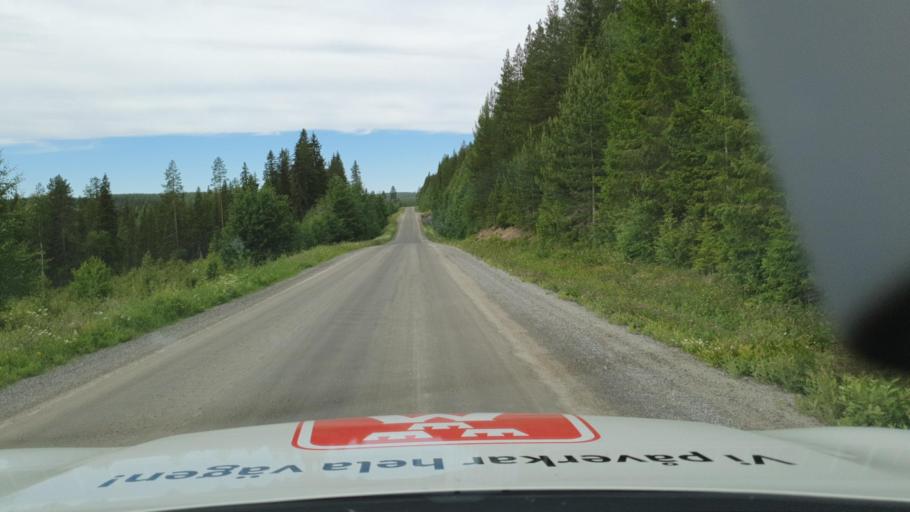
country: SE
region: Vaesterbotten
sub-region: Skelleftea Kommun
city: Burtraesk
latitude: 64.3716
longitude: 20.3757
